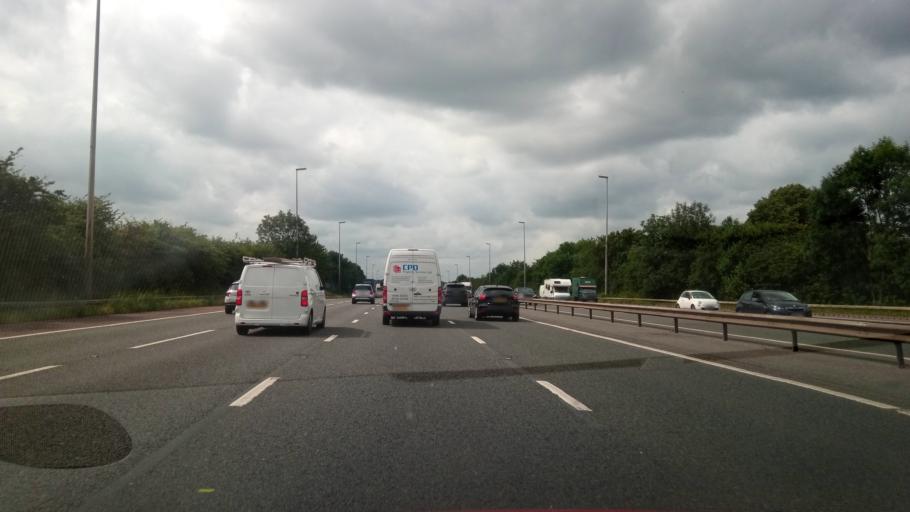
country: GB
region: England
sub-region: Lancashire
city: Clayton-le-Woods
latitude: 53.7526
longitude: -2.6416
